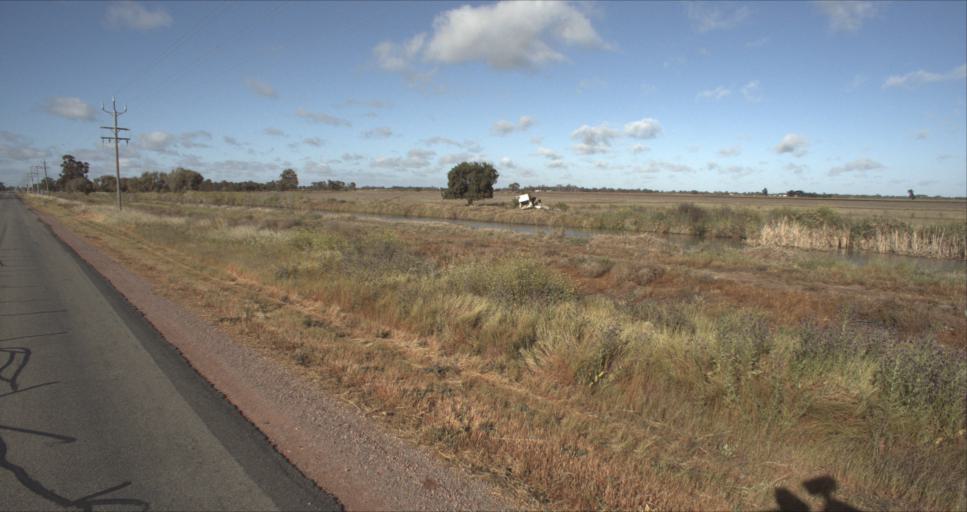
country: AU
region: New South Wales
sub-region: Leeton
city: Leeton
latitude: -34.5272
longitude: 146.3894
